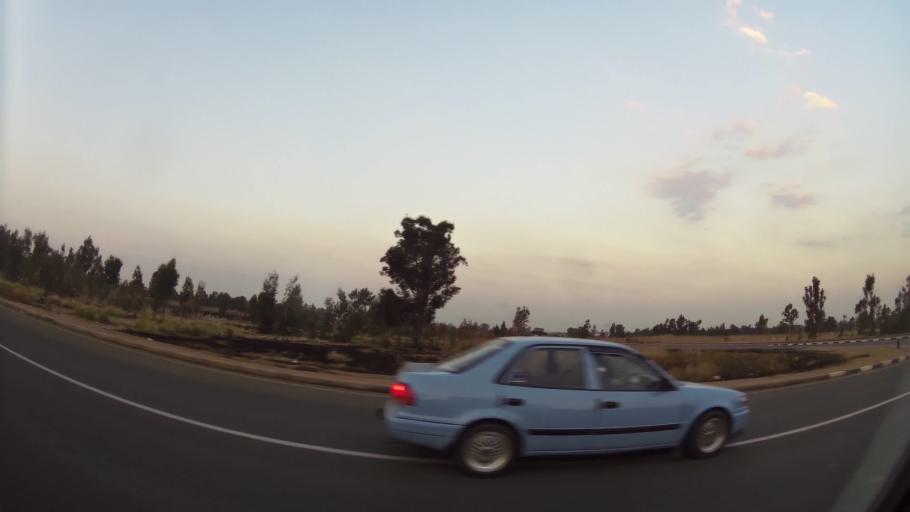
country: ZA
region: Gauteng
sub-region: Ekurhuleni Metropolitan Municipality
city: Springs
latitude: -26.2770
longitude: 28.4295
